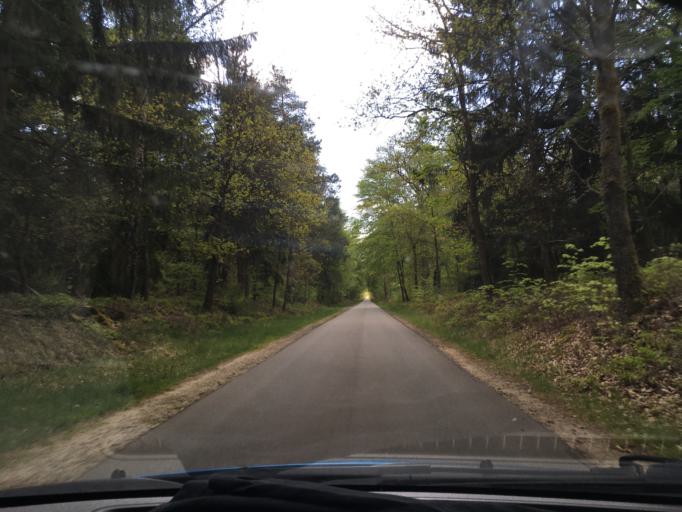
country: DE
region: Lower Saxony
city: Nahrendorf
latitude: 53.1347
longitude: 10.8001
